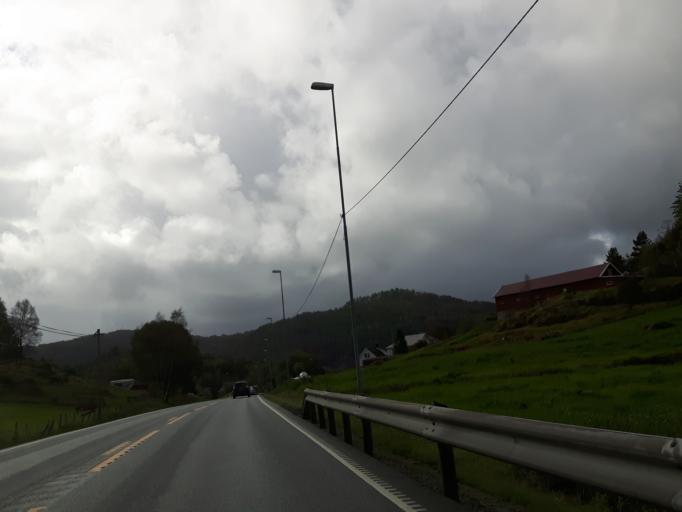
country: NO
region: Vest-Agder
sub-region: Flekkefjord
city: Flekkefjord
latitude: 58.3629
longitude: 6.6354
